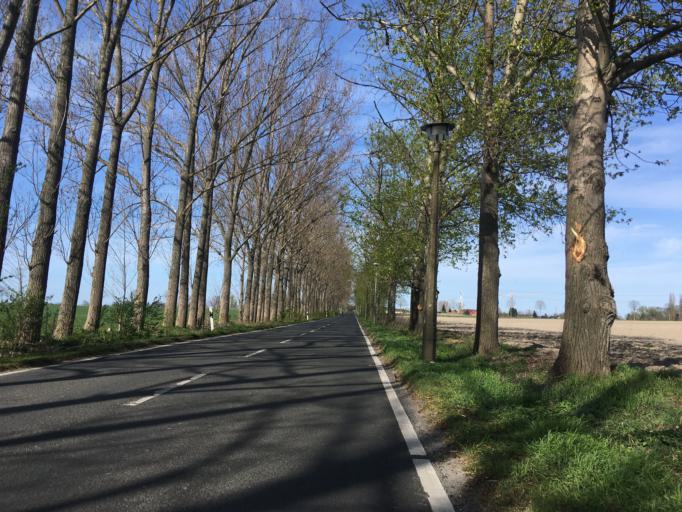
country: DE
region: Berlin
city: Wartenberg
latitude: 52.5871
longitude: 13.5247
